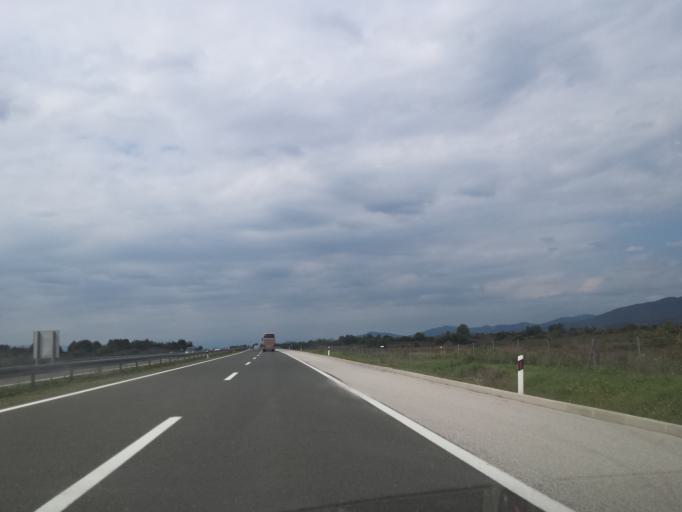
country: HR
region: Licko-Senjska
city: Gospic
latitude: 44.4707
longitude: 15.5899
